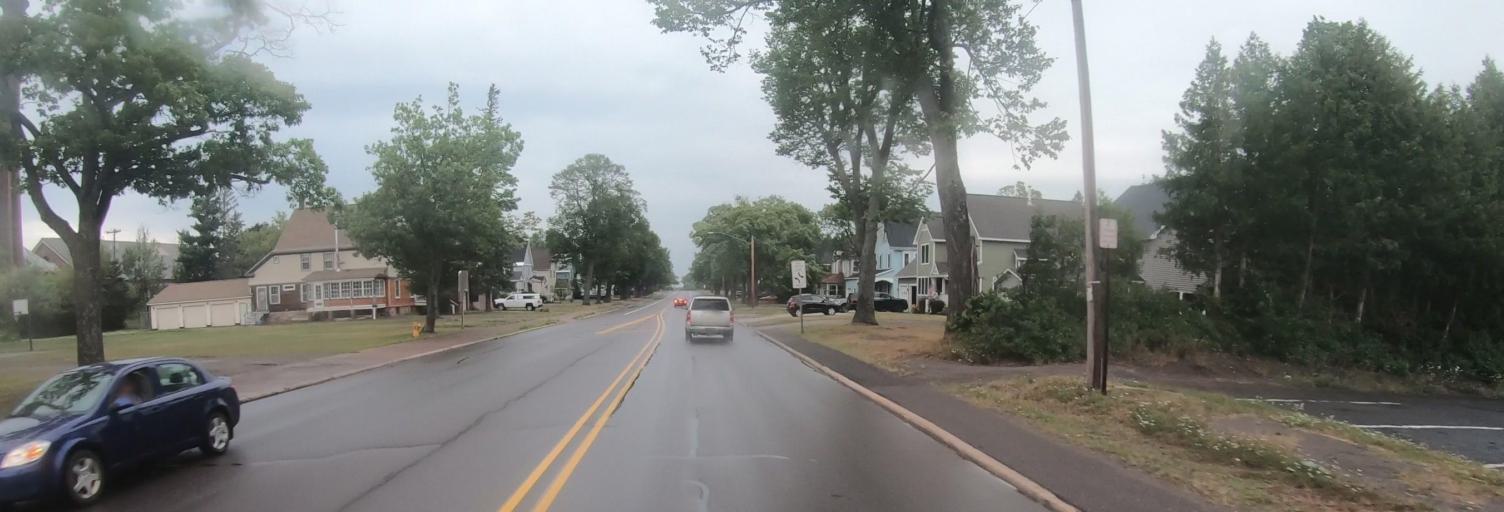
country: US
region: Michigan
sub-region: Houghton County
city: Laurium
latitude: 47.2429
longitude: -88.4462
